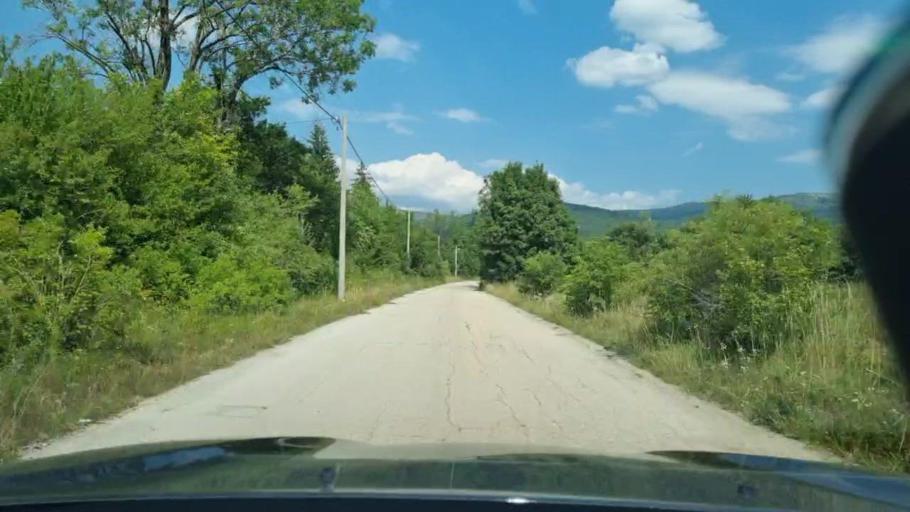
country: BA
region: Federation of Bosnia and Herzegovina
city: Bosansko Grahovo
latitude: 44.2942
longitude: 16.2892
